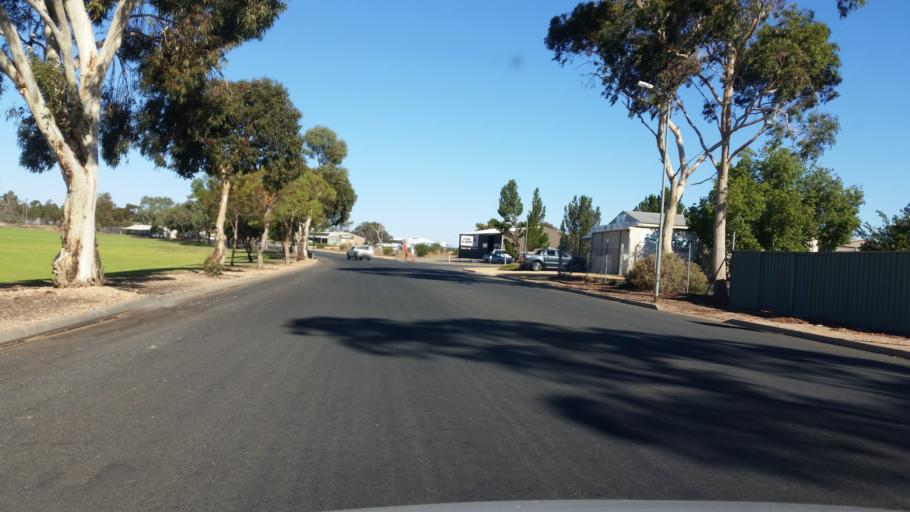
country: AU
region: South Australia
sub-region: Loxton Waikerie
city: Waikerie
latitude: -34.1879
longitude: 139.9776
